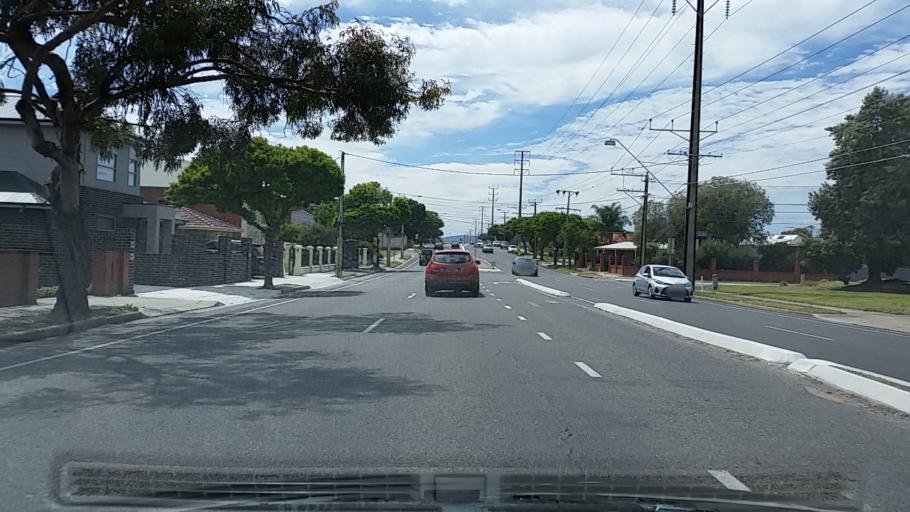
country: AU
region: South Australia
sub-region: Charles Sturt
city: Seaton
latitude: -34.9061
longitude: 138.5193
